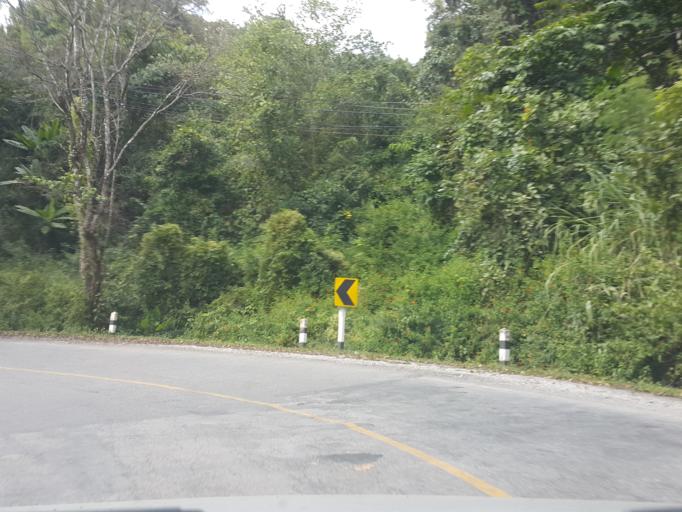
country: TH
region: Mae Hong Son
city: Mae Hi
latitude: 19.2546
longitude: 98.6472
